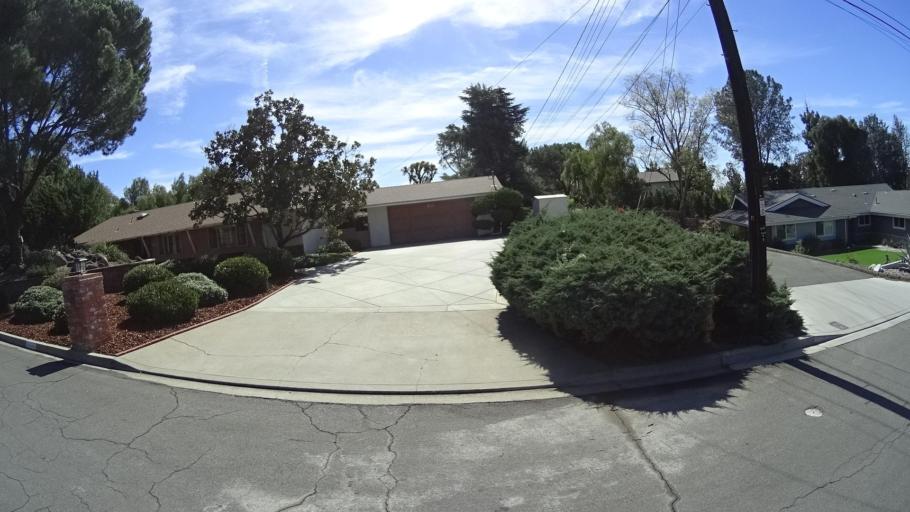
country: US
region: California
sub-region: San Diego County
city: Casa de Oro-Mount Helix
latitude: 32.7567
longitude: -116.9567
